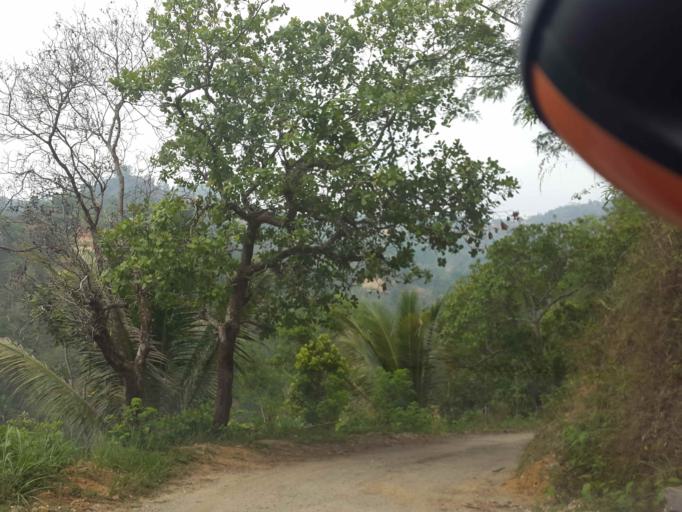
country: ID
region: East Java
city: Ploso
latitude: -8.0512
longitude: 111.1338
